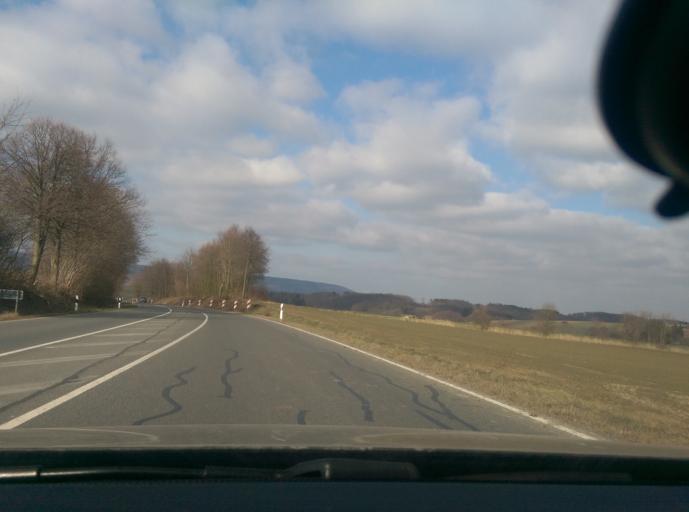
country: DE
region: Lower Saxony
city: Rehren
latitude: 52.2119
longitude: 9.2398
